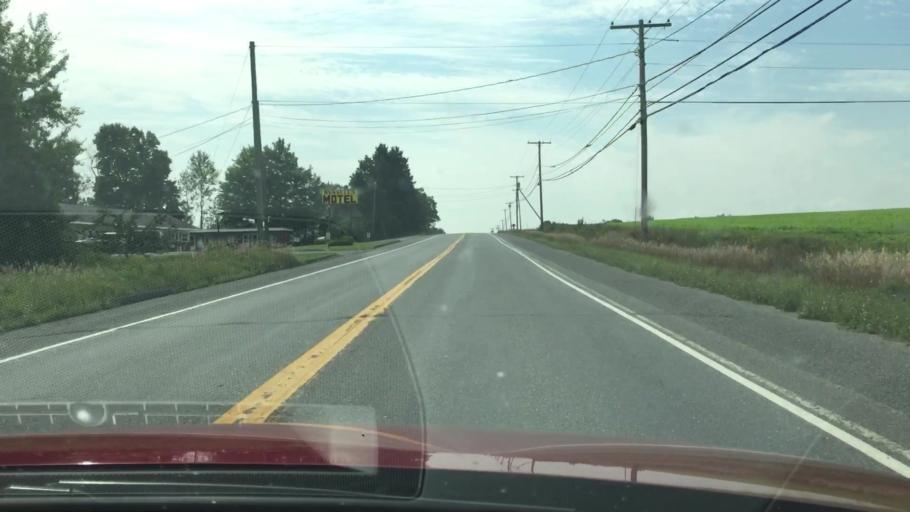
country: US
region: Maine
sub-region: Aroostook County
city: Caribou
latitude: 46.8369
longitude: -68.0103
